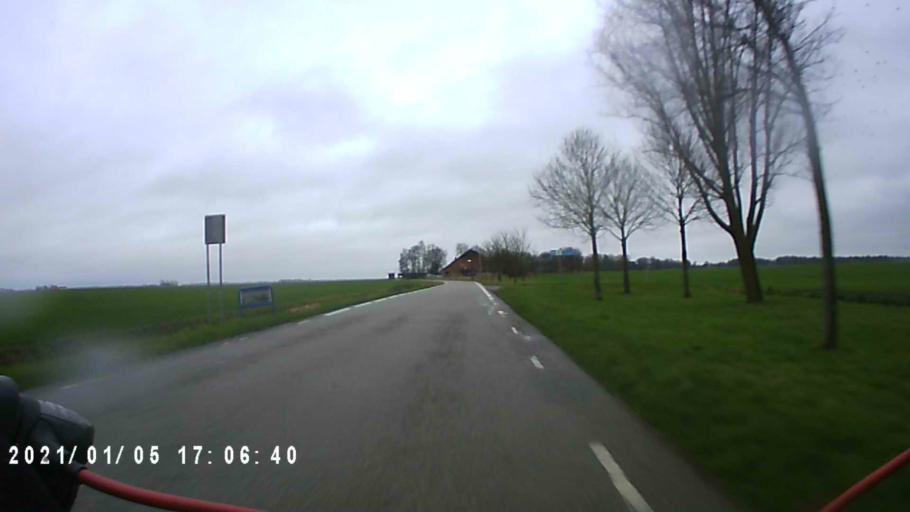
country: NL
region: Groningen
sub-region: Gemeente  Oldambt
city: Winschoten
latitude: 53.2538
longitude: 7.0224
